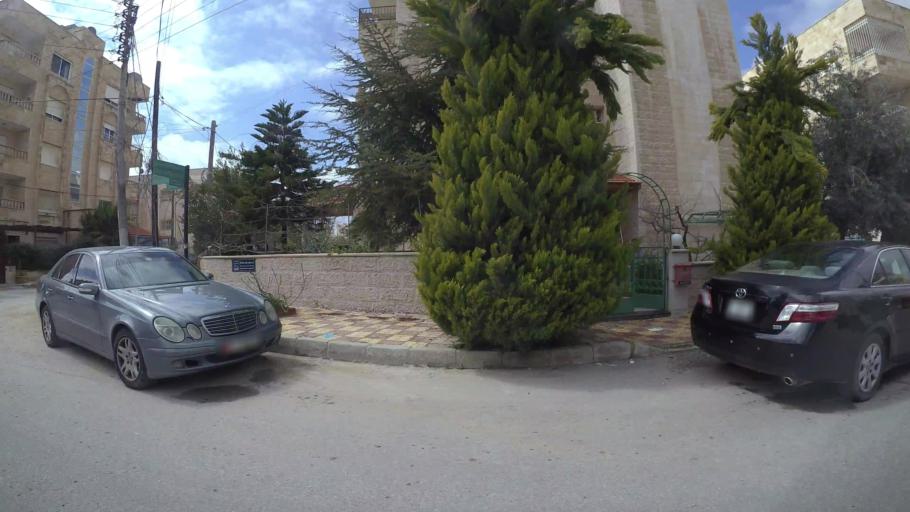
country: JO
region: Amman
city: Al Jubayhah
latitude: 31.9912
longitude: 35.8474
